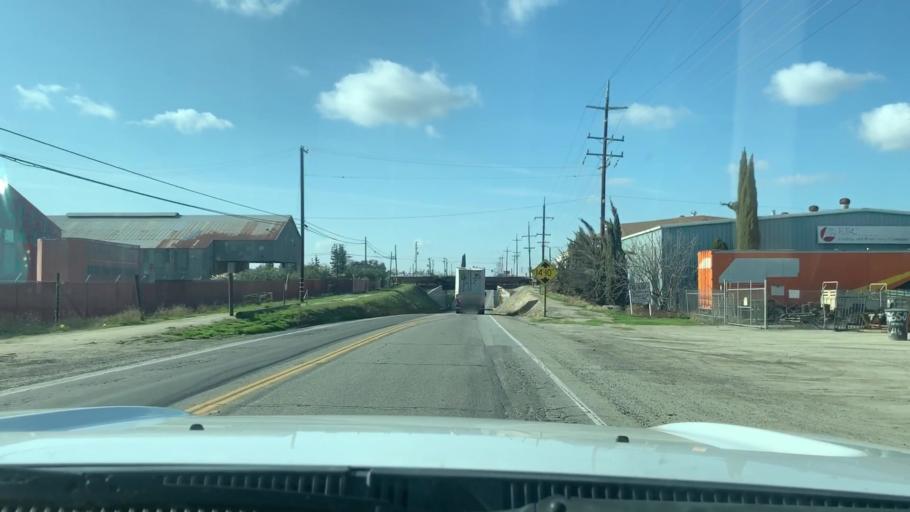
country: US
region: California
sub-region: Kern County
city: Wasco
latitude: 35.6016
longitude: -119.3297
